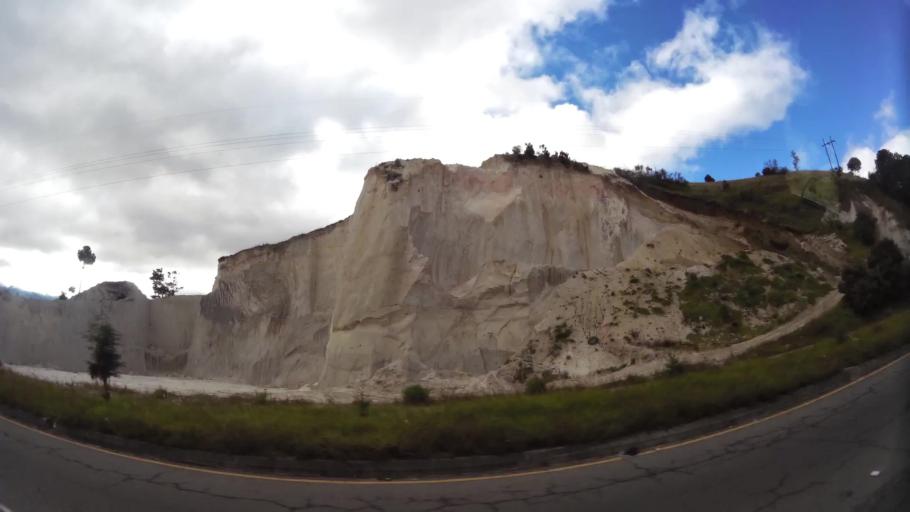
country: GT
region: Quetzaltenango
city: Salcaja
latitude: 14.8716
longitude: -91.4695
